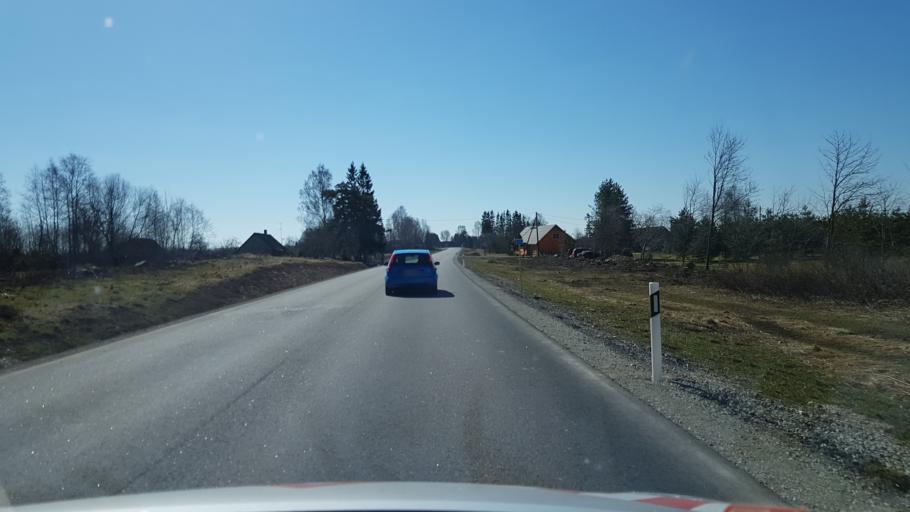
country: EE
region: Laeaene-Virumaa
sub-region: Vinni vald
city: Vinni
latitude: 59.1089
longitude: 26.6184
